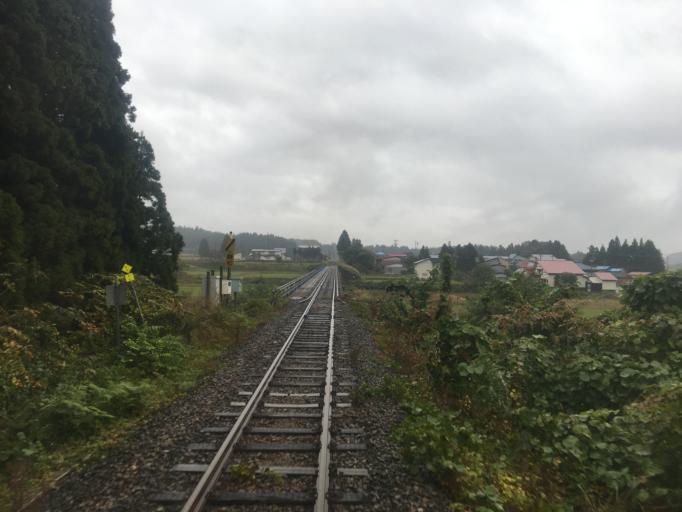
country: JP
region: Yamagata
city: Shinjo
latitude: 38.7650
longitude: 140.4492
